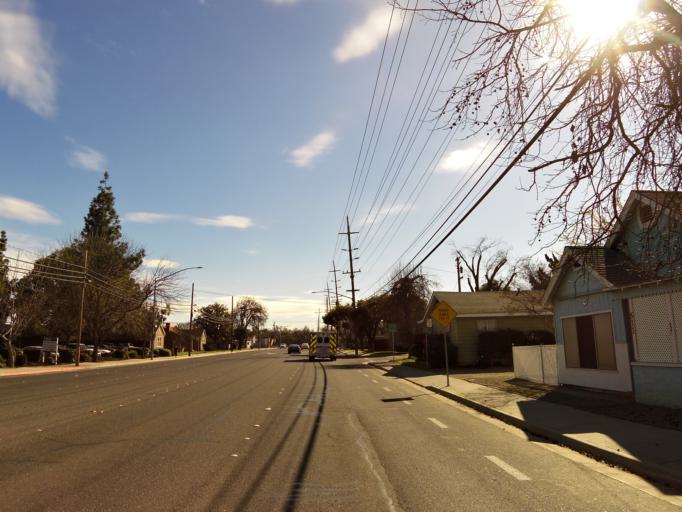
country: US
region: California
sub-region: Stanislaus County
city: Modesto
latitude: 37.6519
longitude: -120.9755
